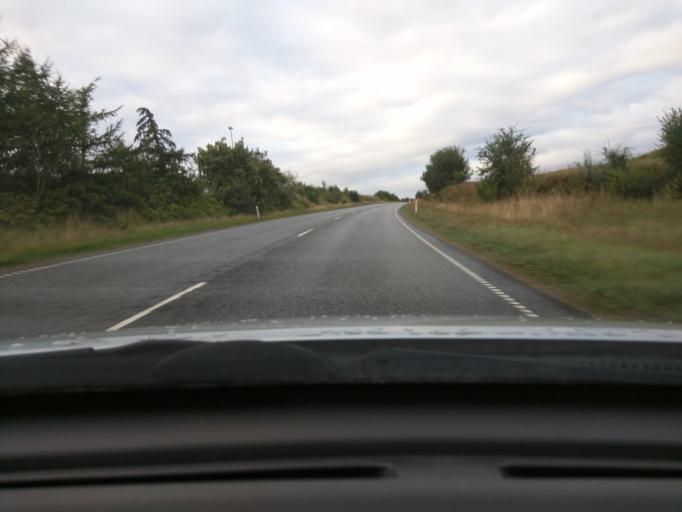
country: DK
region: Central Jutland
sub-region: Silkeborg Kommune
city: Kjellerup
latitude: 56.3227
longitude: 9.3329
